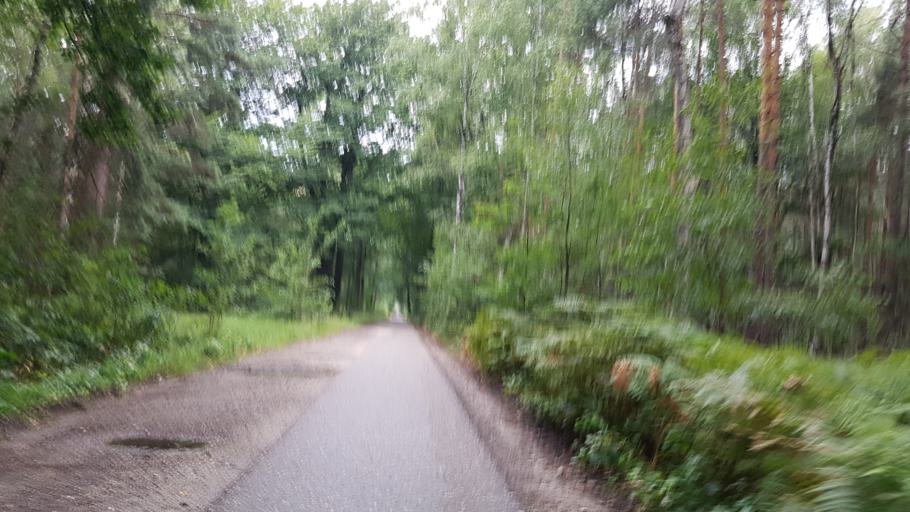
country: DE
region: Brandenburg
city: Schonborn
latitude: 51.6214
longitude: 13.4682
